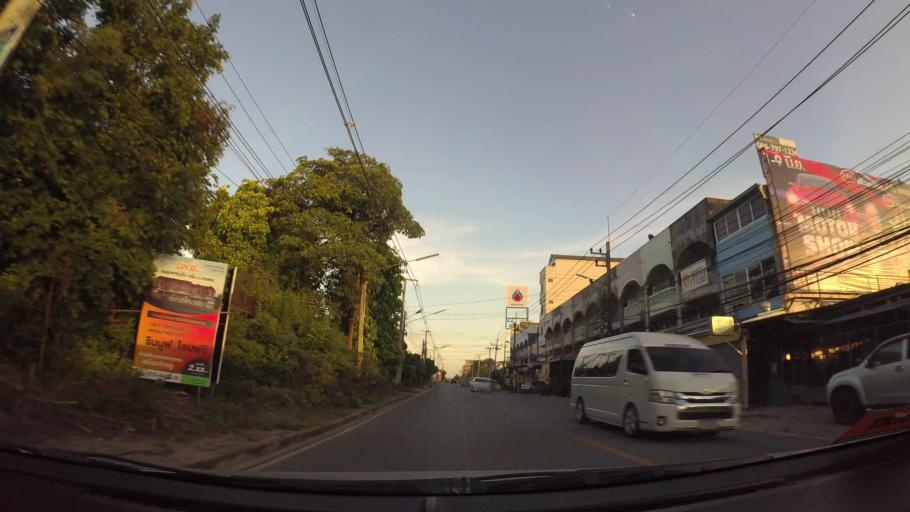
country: TH
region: Chon Buri
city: Si Racha
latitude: 13.1166
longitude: 100.9468
